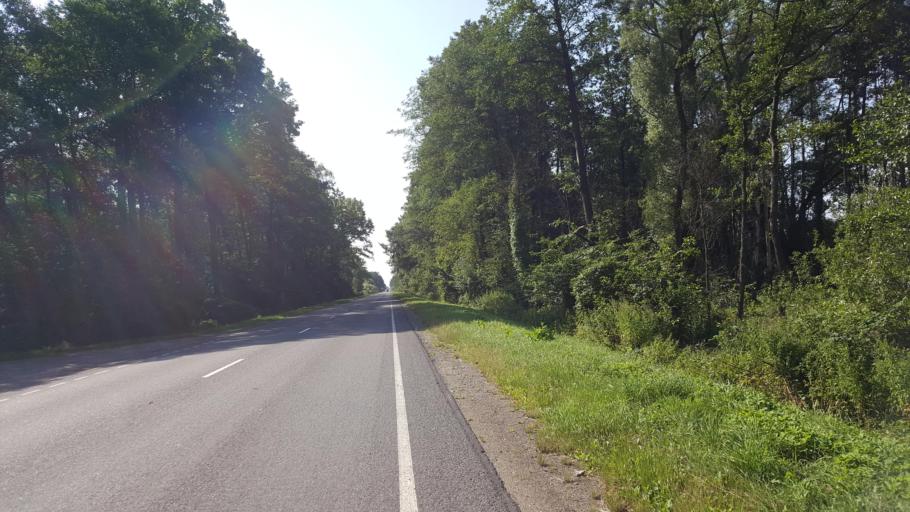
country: BY
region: Brest
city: Zhabinka
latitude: 52.2792
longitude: 23.9492
